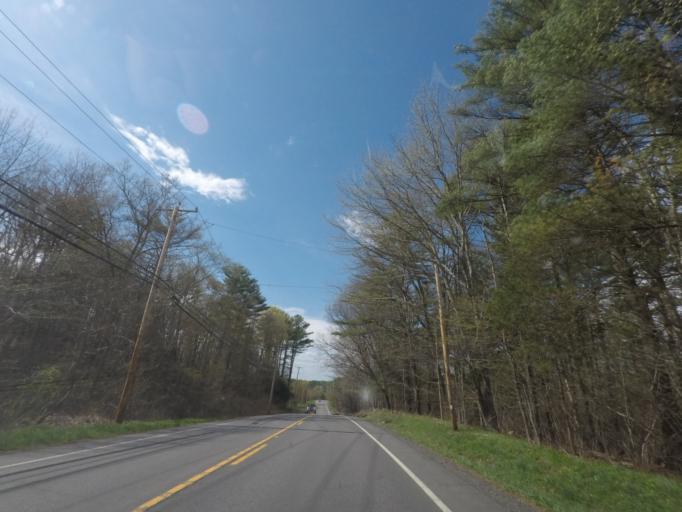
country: US
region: New York
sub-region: Greene County
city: Cairo
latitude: 42.3125
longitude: -74.0082
